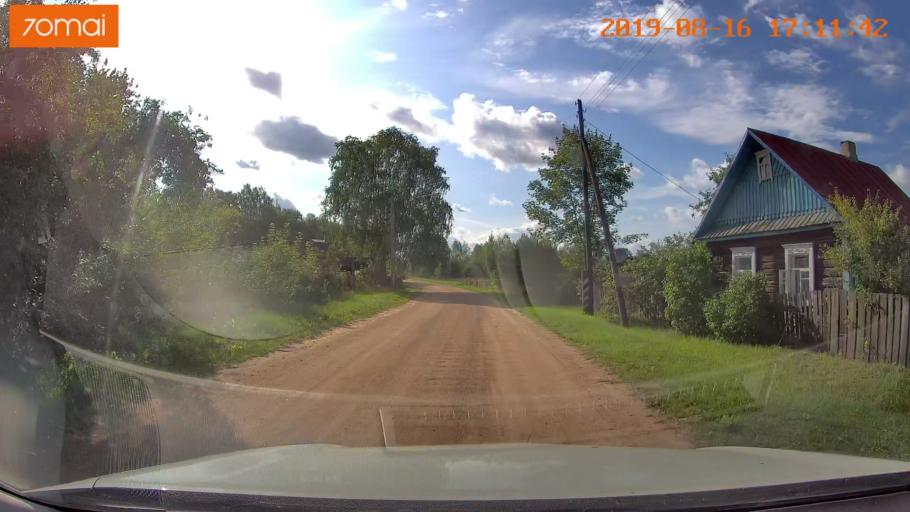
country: BY
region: Mogilev
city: Hlusha
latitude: 53.1964
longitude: 28.9024
